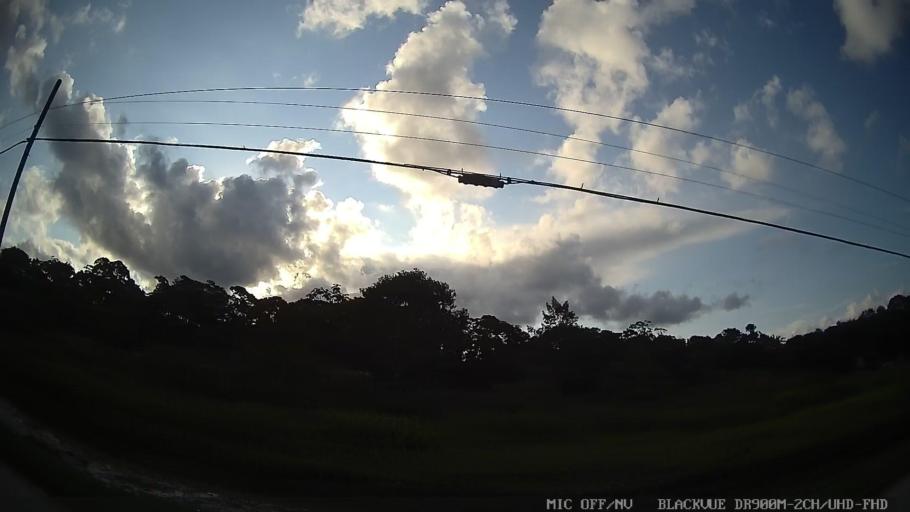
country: BR
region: Sao Paulo
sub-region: Itanhaem
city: Itanhaem
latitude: -24.1583
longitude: -46.8293
